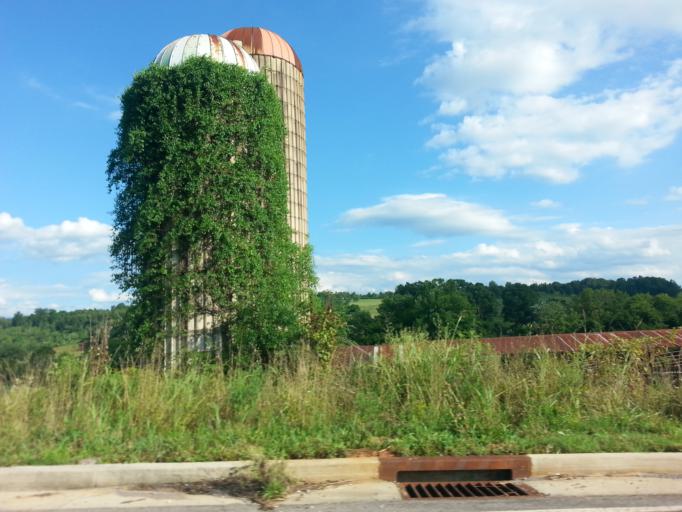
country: US
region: Tennessee
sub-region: Loudon County
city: Greenback
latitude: 35.6573
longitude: -84.1026
